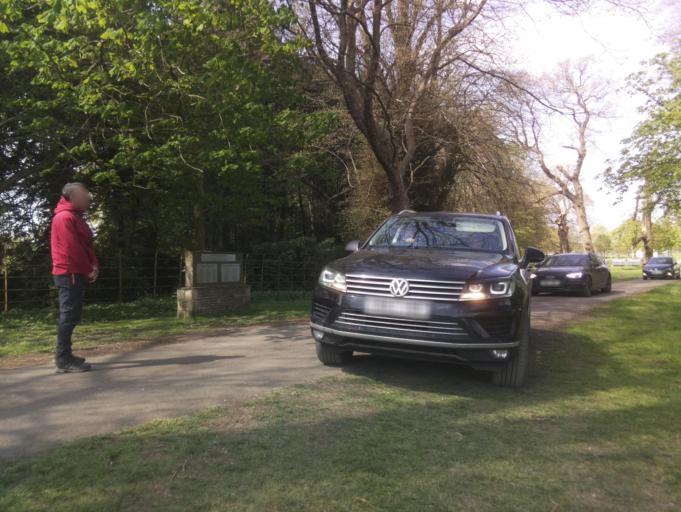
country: GB
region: England
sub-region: Wiltshire
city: Luckington
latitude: 51.5455
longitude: -2.2814
